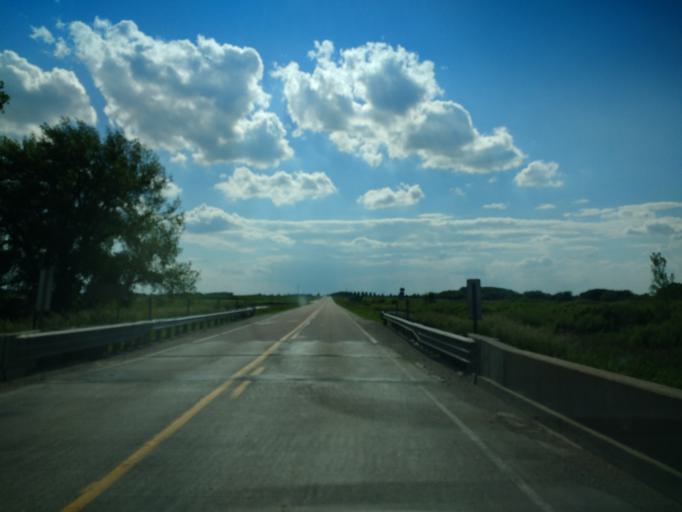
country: US
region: Iowa
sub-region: Clay County
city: Spencer
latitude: 43.1843
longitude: -95.1919
